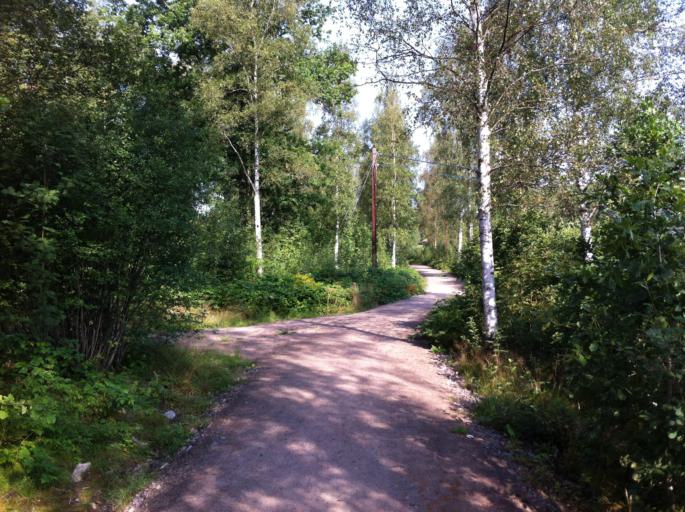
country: SE
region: Halland
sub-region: Hylte Kommun
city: Hyltebruk
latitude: 57.0028
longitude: 13.2462
